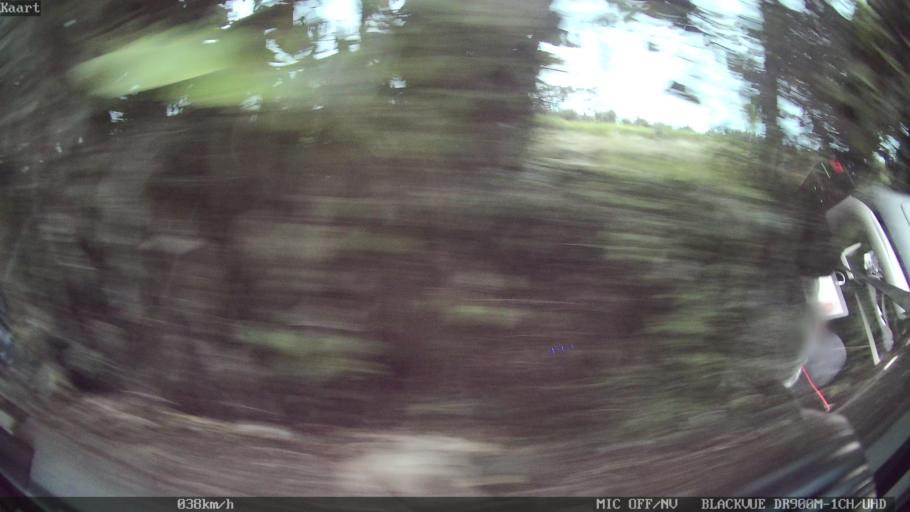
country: ID
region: Bali
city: Banjar Cemenggon
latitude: -8.5428
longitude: 115.2113
